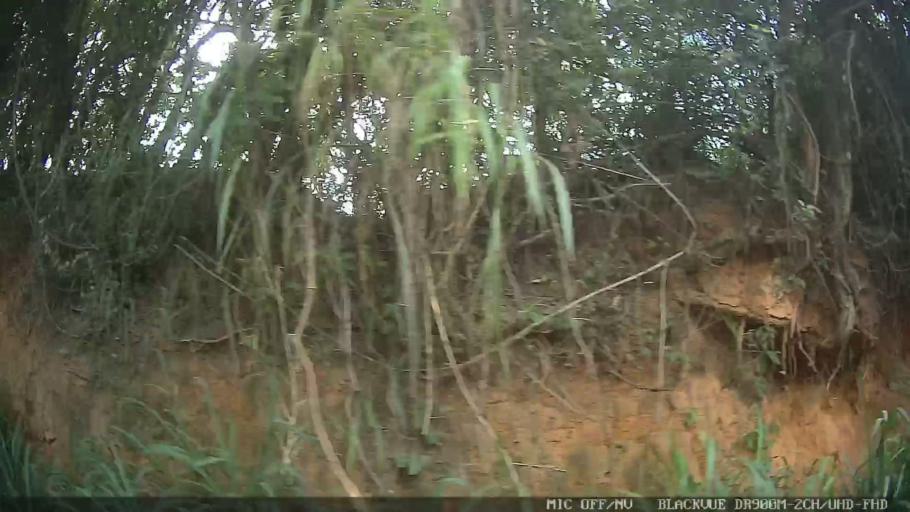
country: BR
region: Sao Paulo
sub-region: Atibaia
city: Atibaia
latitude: -23.1093
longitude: -46.6070
